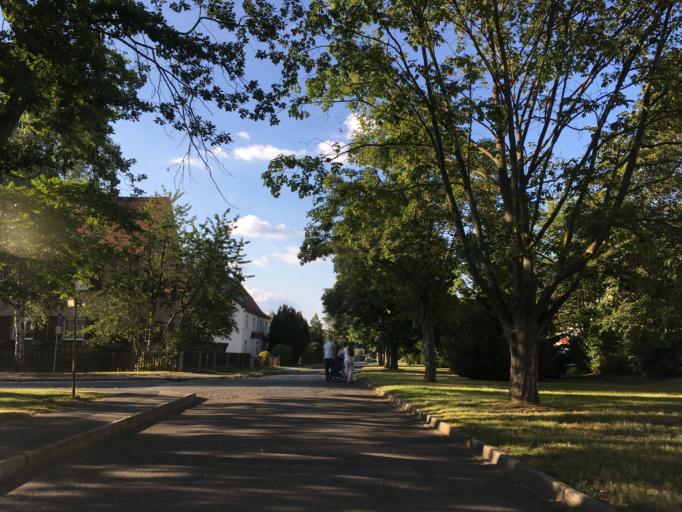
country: DE
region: Saxony
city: Radeberg
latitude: 51.1050
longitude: 13.9178
